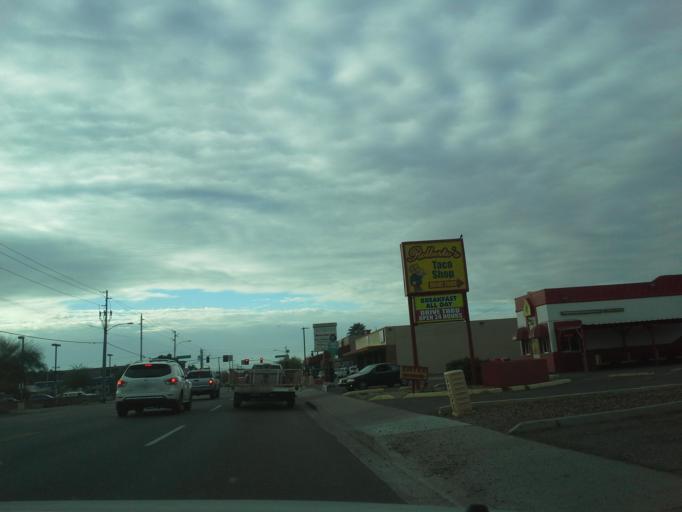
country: US
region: Arizona
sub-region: Maricopa County
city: Phoenix
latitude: 33.5107
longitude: -112.0651
